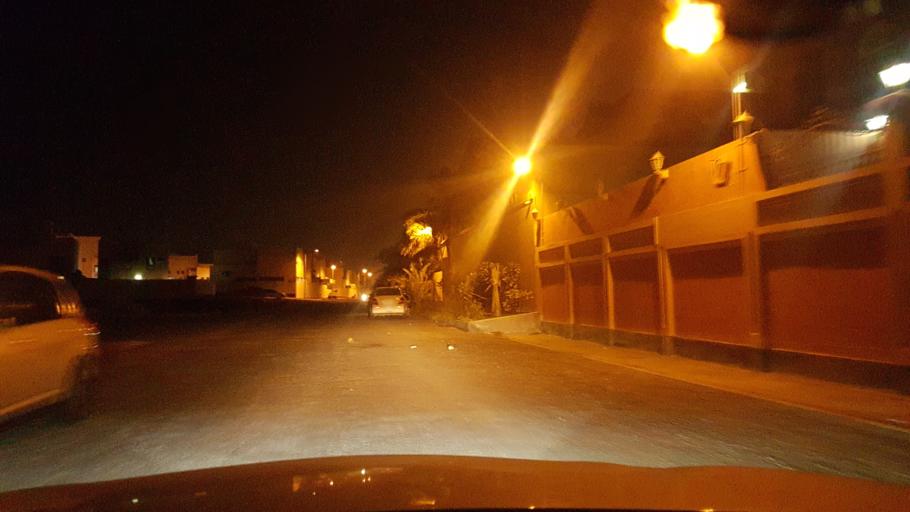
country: BH
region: Central Governorate
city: Madinat Hamad
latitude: 26.0937
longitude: 50.4863
